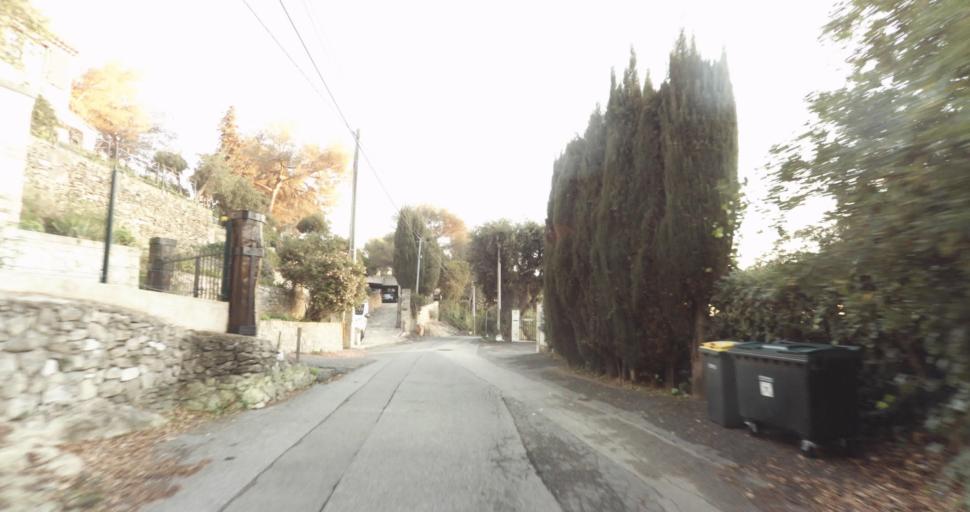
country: FR
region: Provence-Alpes-Cote d'Azur
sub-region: Departement des Alpes-Maritimes
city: La Gaude
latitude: 43.7292
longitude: 7.1339
